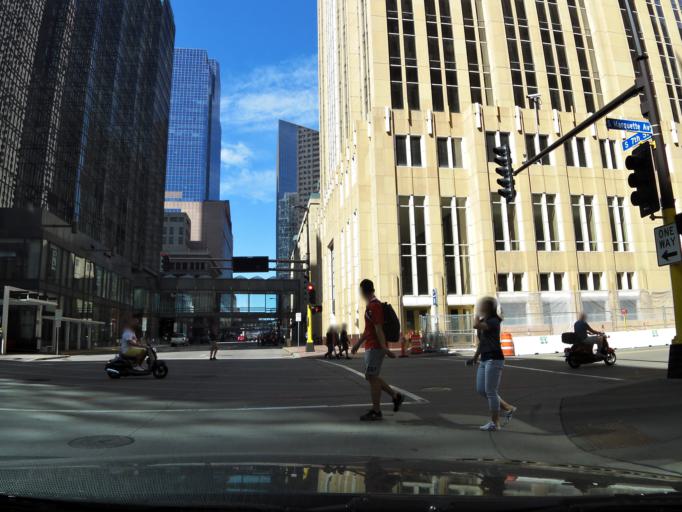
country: US
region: Minnesota
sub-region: Hennepin County
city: Minneapolis
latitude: 44.9763
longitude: -93.2706
